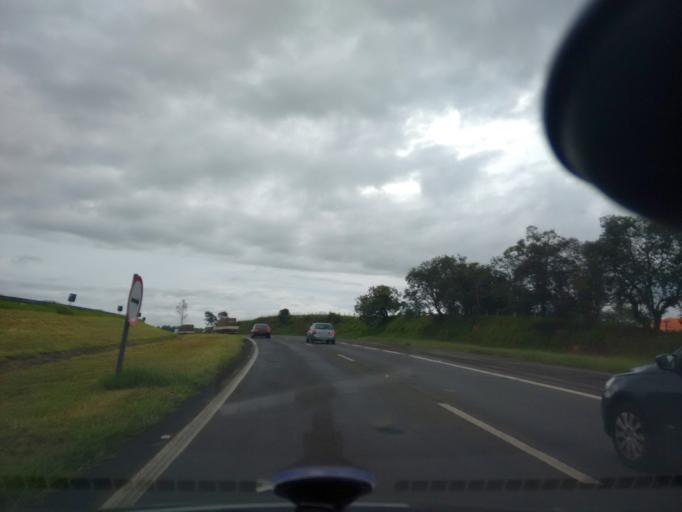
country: BR
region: Sao Paulo
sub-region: Rio Claro
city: Rio Claro
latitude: -22.3239
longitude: -47.6563
